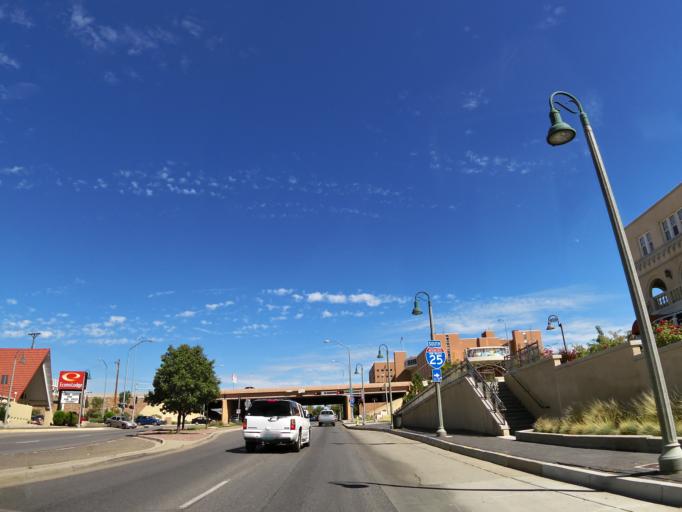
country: US
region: New Mexico
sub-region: Bernalillo County
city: Albuquerque
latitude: 35.0828
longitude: -106.6383
